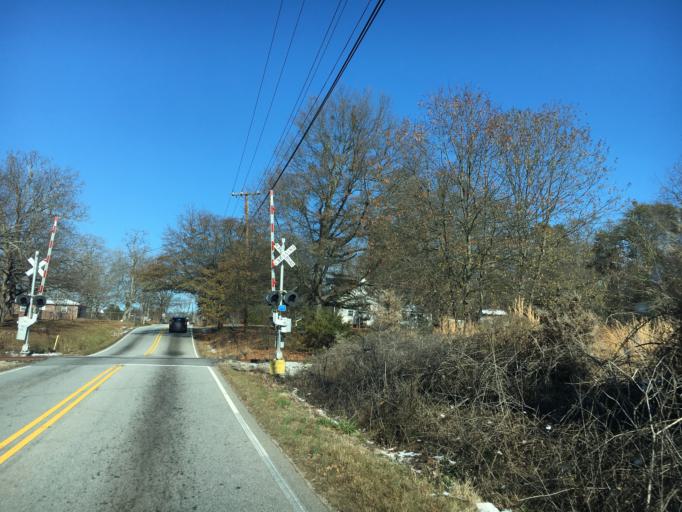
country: US
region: South Carolina
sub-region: Greenville County
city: Taylors
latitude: 34.9301
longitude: -82.2691
